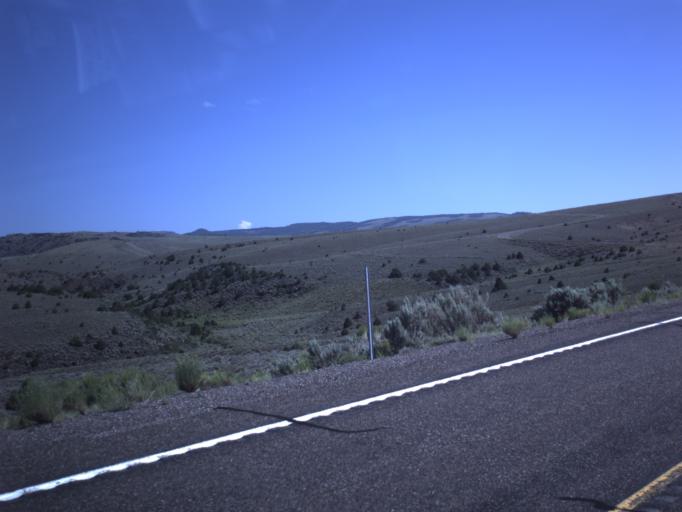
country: US
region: Utah
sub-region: Wayne County
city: Loa
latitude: 38.5279
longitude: -111.5172
